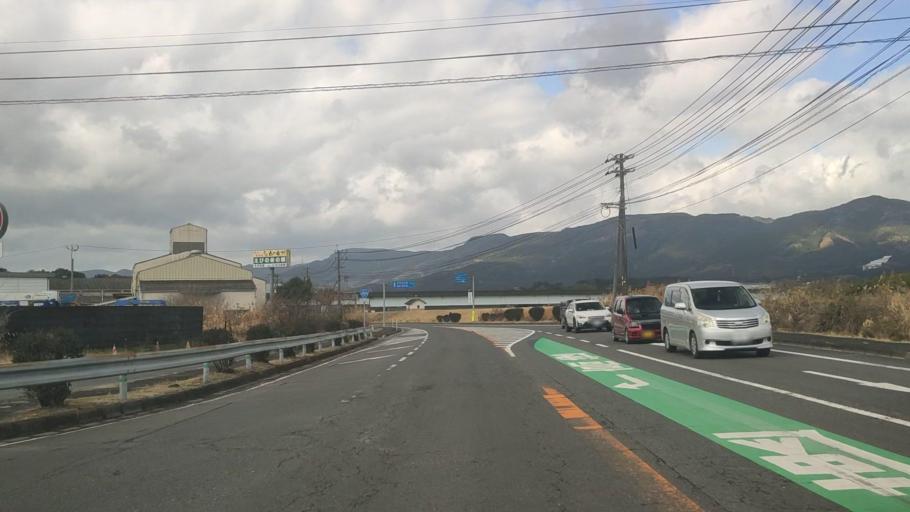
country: JP
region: Kumamoto
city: Hitoyoshi
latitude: 32.0521
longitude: 130.8042
